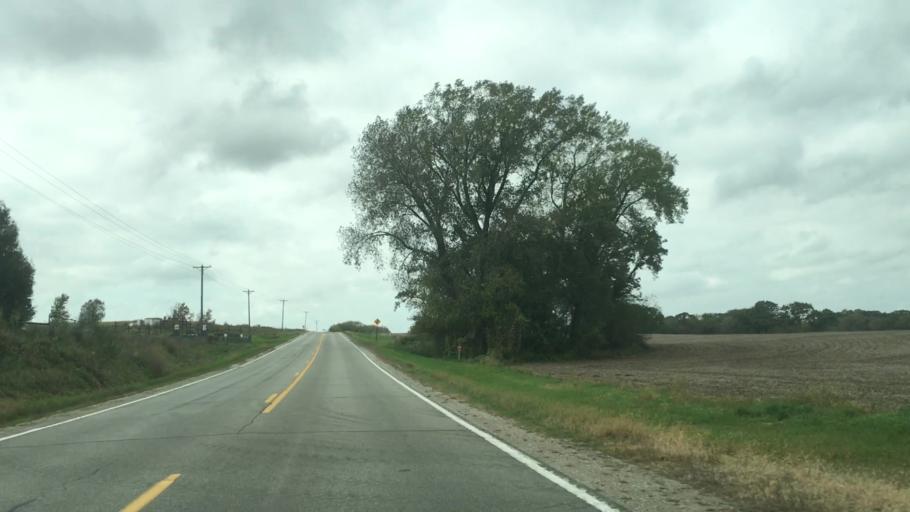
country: US
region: Minnesota
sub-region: Fillmore County
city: Preston
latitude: 43.7353
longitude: -92.1189
